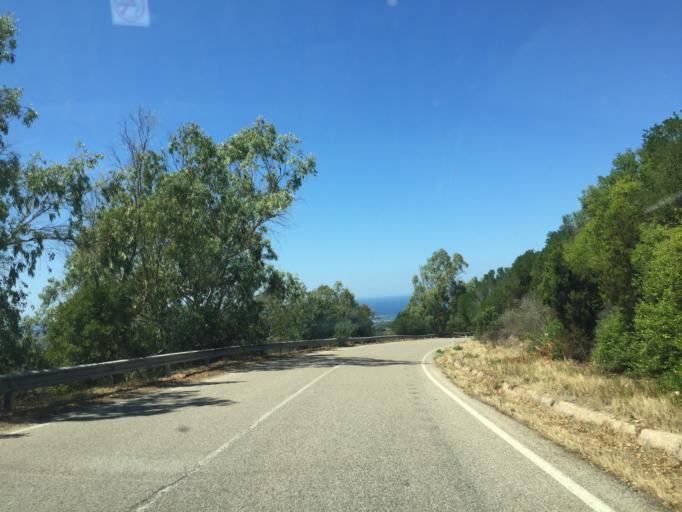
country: IT
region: Sardinia
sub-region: Provincia di Olbia-Tempio
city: Aglientu
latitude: 41.0902
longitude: 9.0981
